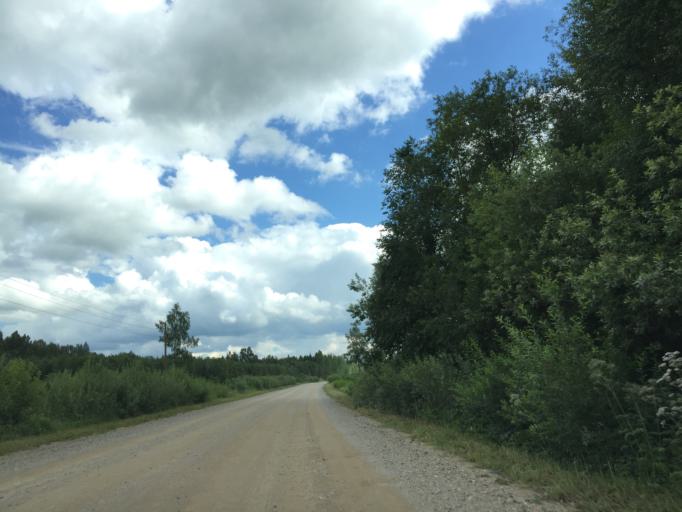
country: LV
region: Malpils
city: Malpils
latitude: 56.8780
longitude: 24.9966
